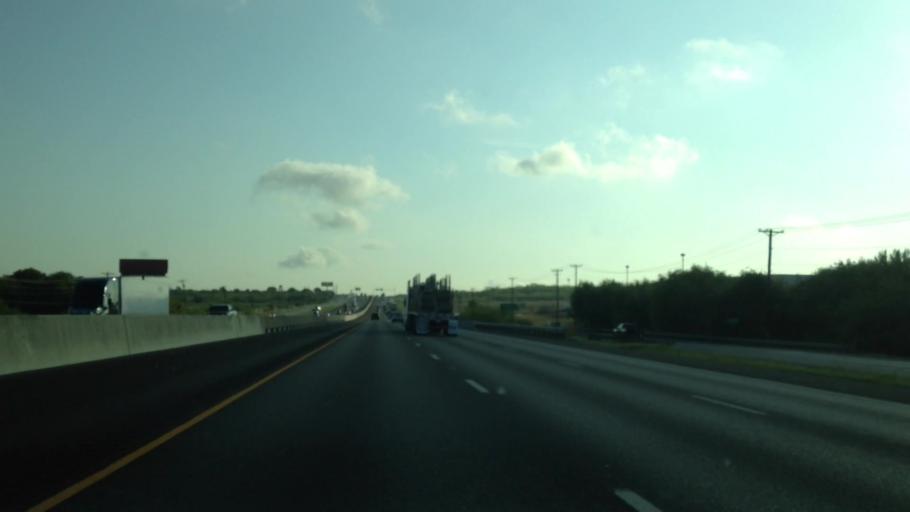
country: US
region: Texas
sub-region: Guadalupe County
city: Lake Dunlap
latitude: 29.7358
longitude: -98.0688
